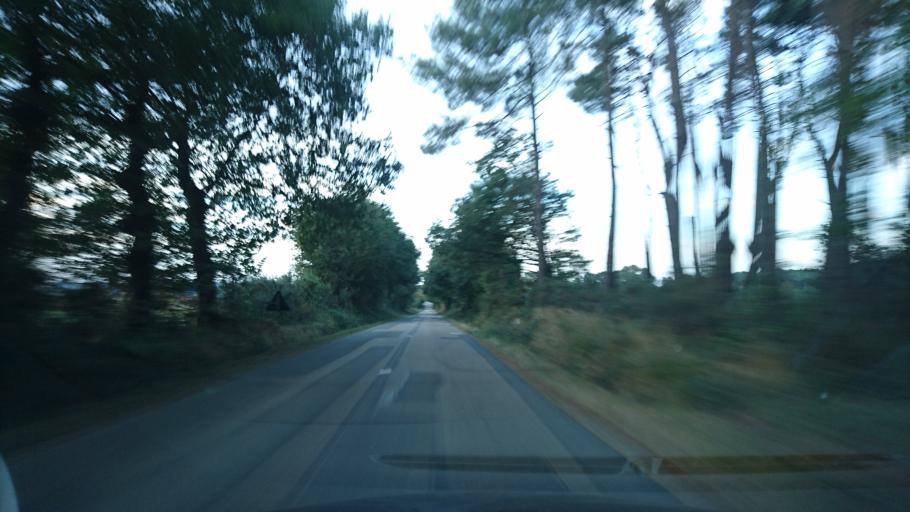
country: FR
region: Brittany
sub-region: Departement d'Ille-et-Vilaine
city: Saint-Just
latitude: 47.7997
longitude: -2.0094
